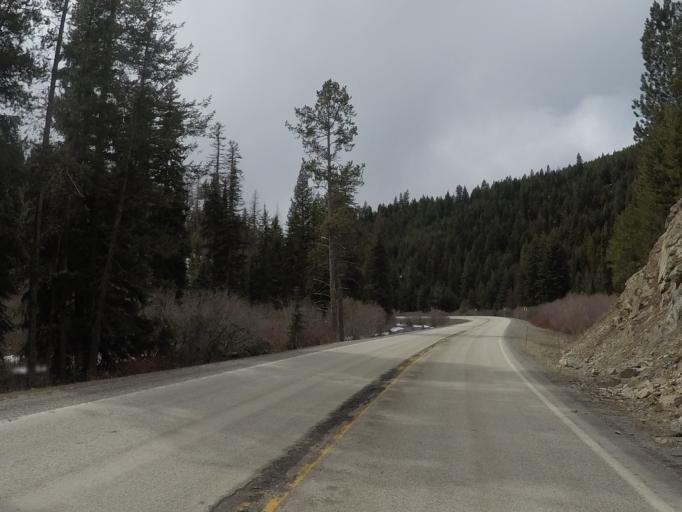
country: US
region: Montana
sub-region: Missoula County
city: Frenchtown
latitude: 46.7568
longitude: -114.4958
